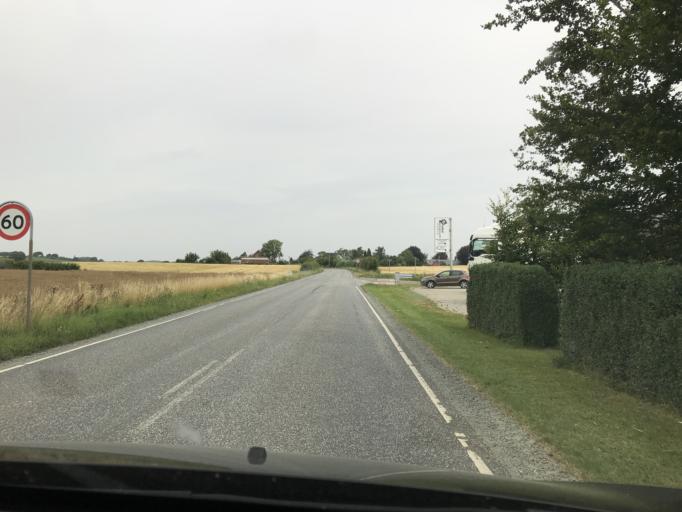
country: DK
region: South Denmark
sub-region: Assens Kommune
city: Arup
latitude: 55.3288
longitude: 10.0505
